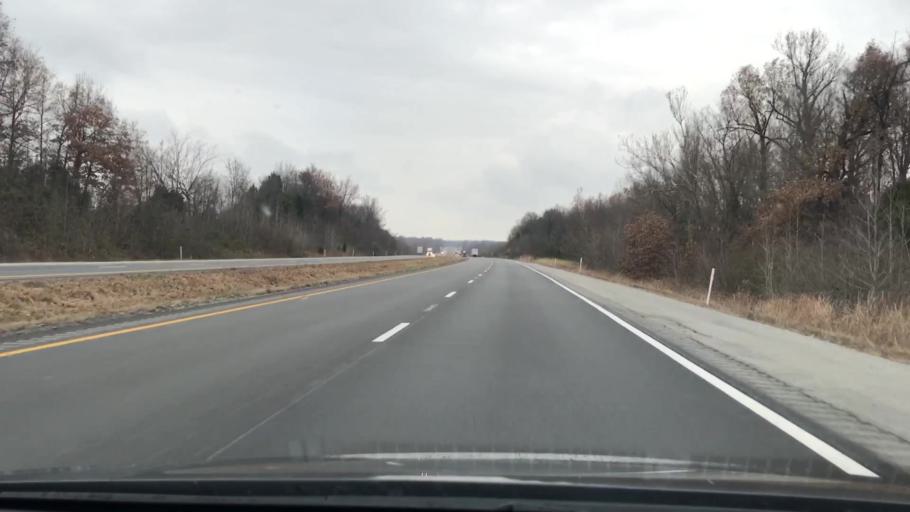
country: US
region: Kentucky
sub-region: Hopkins County
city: Madisonville
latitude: 37.4310
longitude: -87.4719
